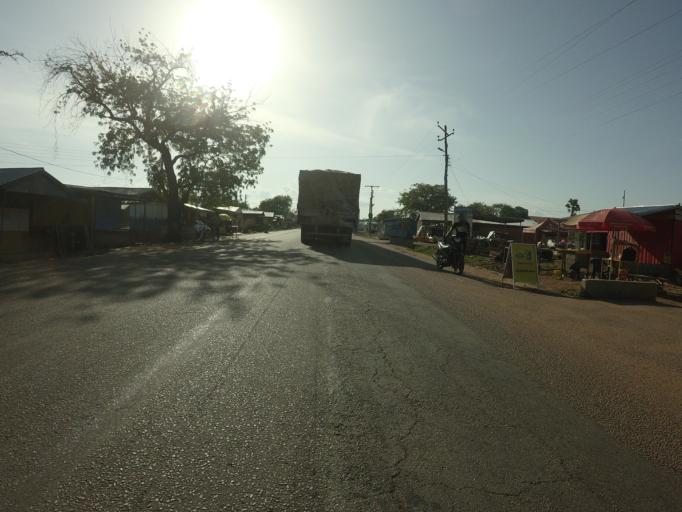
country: GH
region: Upper East
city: Navrongo
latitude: 10.8953
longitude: -1.0842
